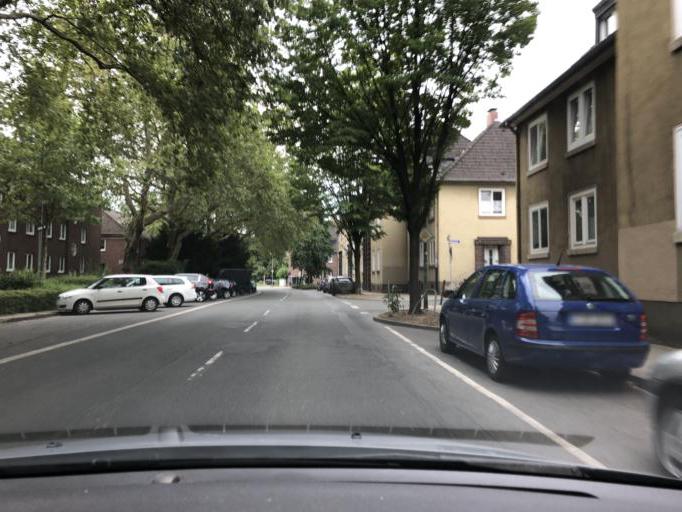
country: DE
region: North Rhine-Westphalia
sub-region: Regierungsbezirk Munster
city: Bottrop
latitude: 51.4736
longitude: 6.9417
